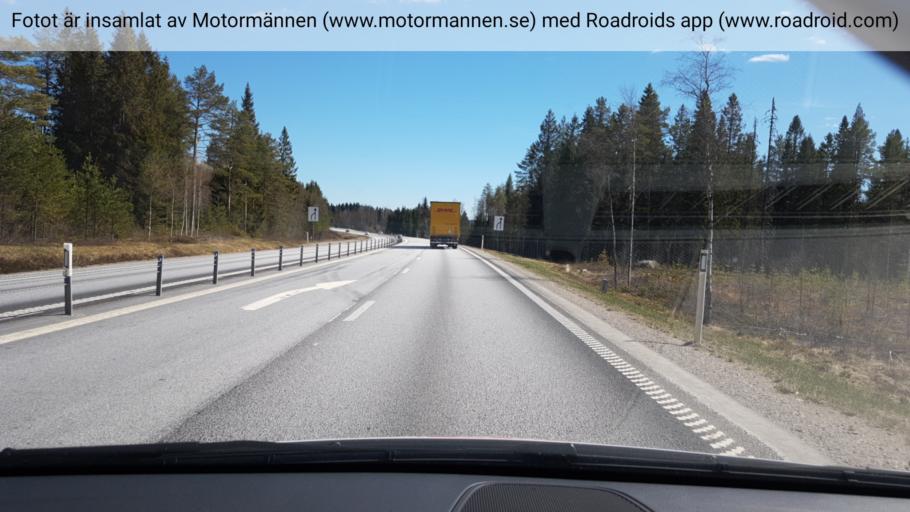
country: SE
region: Vaesterbotten
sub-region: Vannas Kommun
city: Vannasby
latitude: 63.9042
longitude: 19.8936
